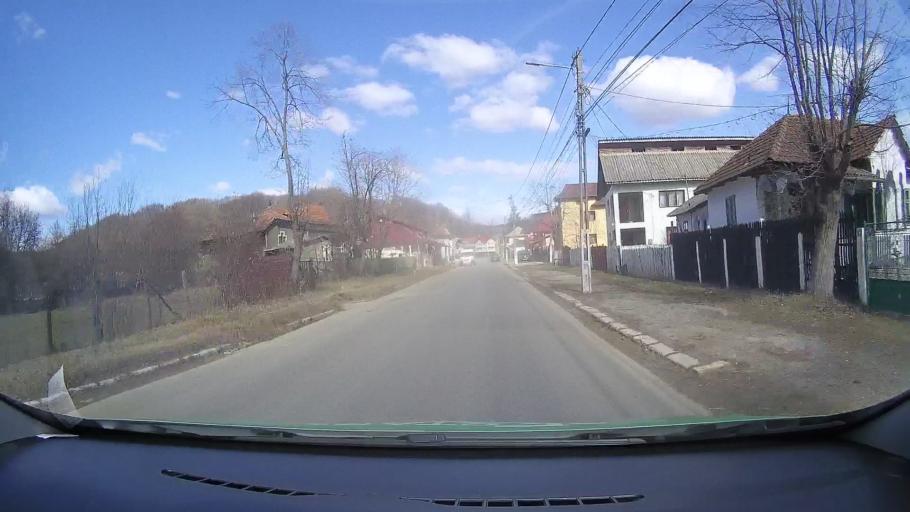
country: RO
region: Dambovita
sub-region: Comuna Vulcana Bai
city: Vulcana Bai
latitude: 45.0725
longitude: 25.3787
